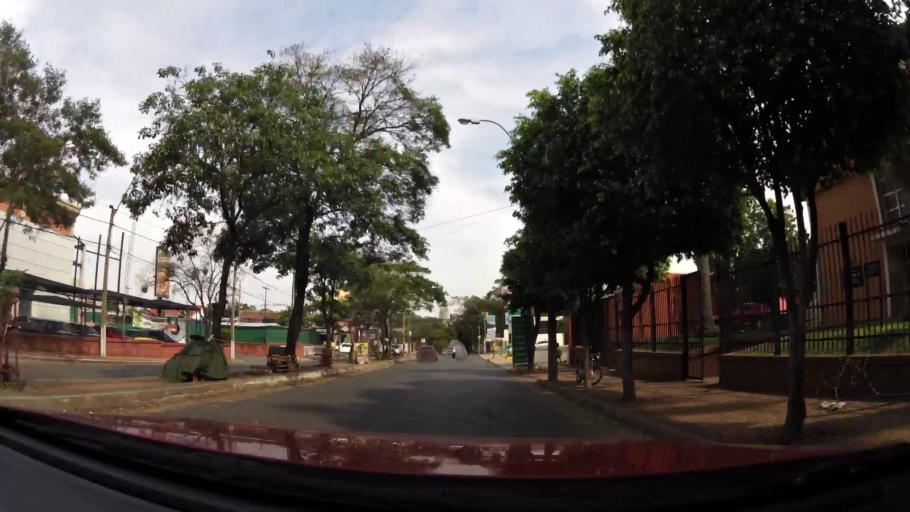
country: PY
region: Asuncion
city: Asuncion
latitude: -25.2700
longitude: -57.5631
